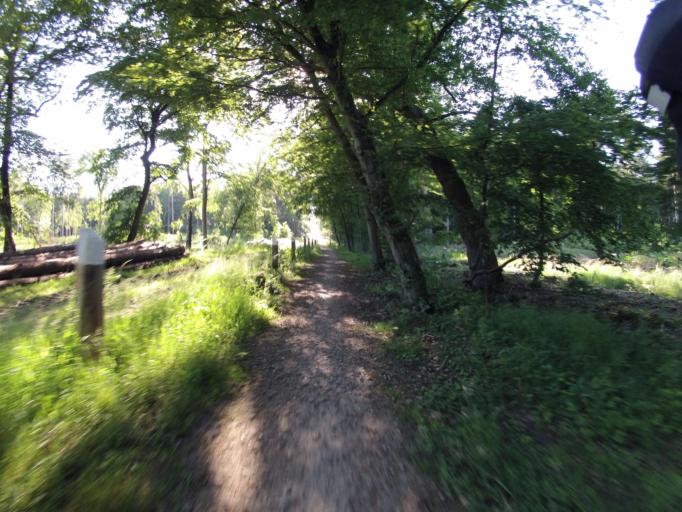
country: DE
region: Lower Saxony
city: Ohne
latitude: 52.3086
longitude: 7.2831
